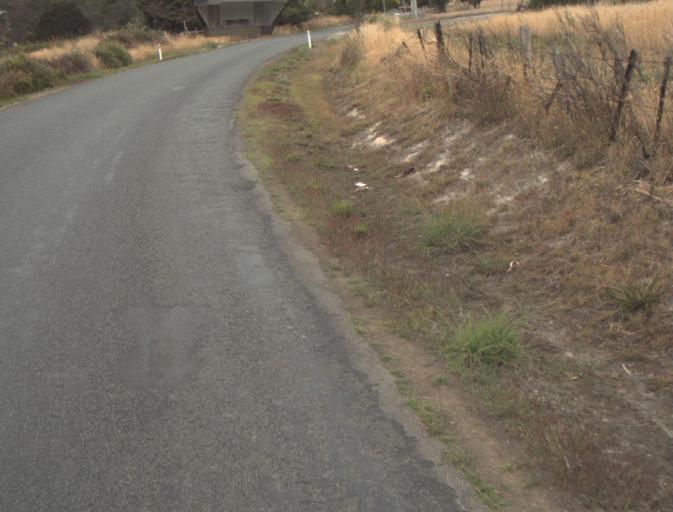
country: AU
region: Tasmania
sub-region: Launceston
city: Mayfield
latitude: -41.2371
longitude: 147.1822
